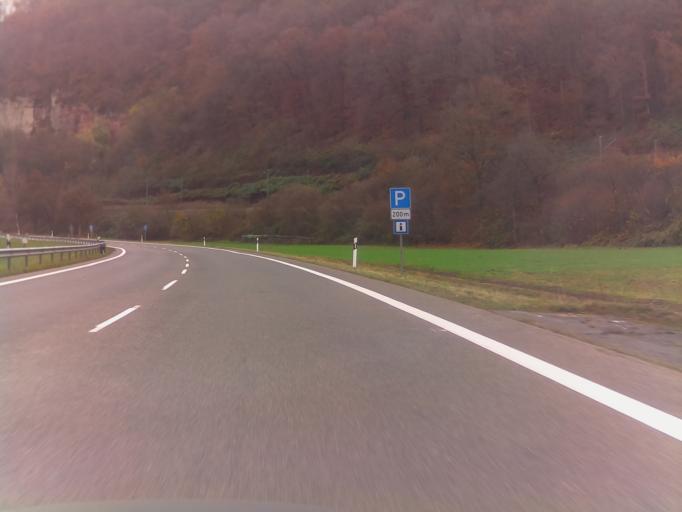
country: DE
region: Baden-Wuerttemberg
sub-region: Karlsruhe Region
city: Eberbach
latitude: 49.4425
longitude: 9.0066
